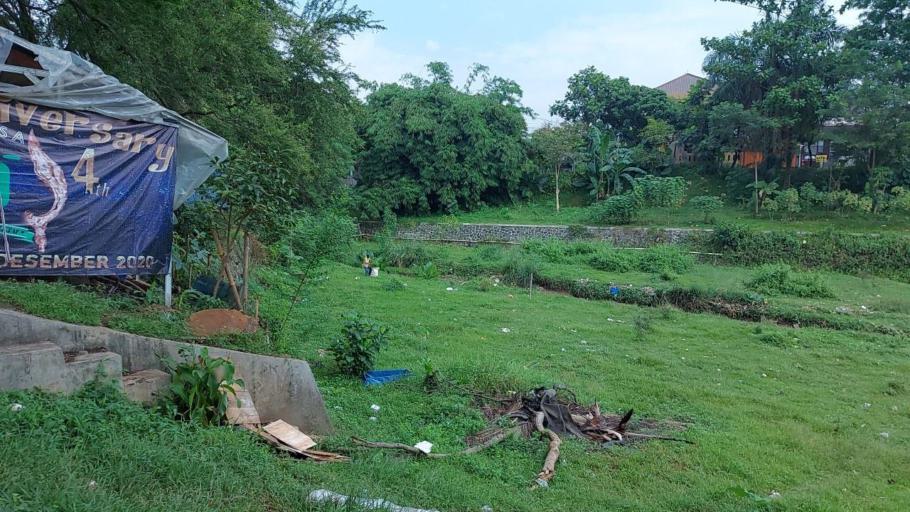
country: ID
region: West Java
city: Bogor
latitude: -6.5422
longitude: 106.8164
